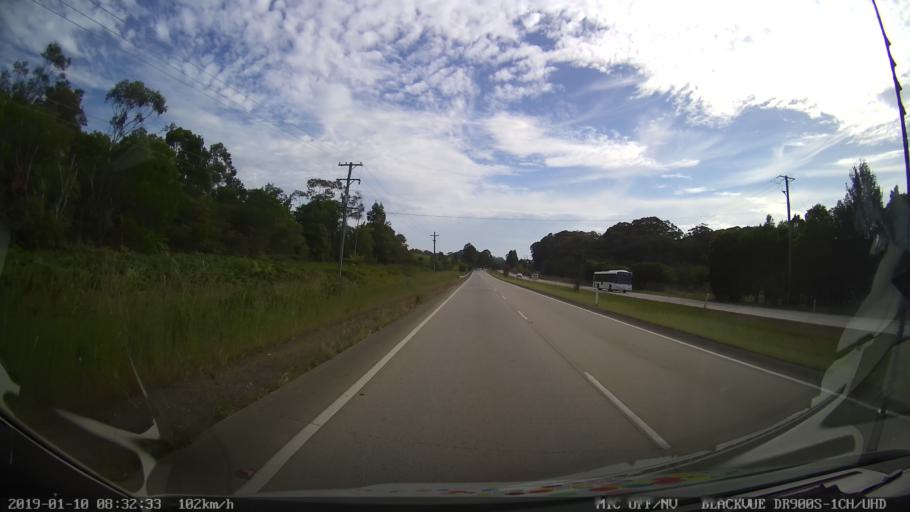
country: AU
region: New South Wales
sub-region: Coffs Harbour
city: Boambee
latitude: -30.3424
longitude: 153.0715
